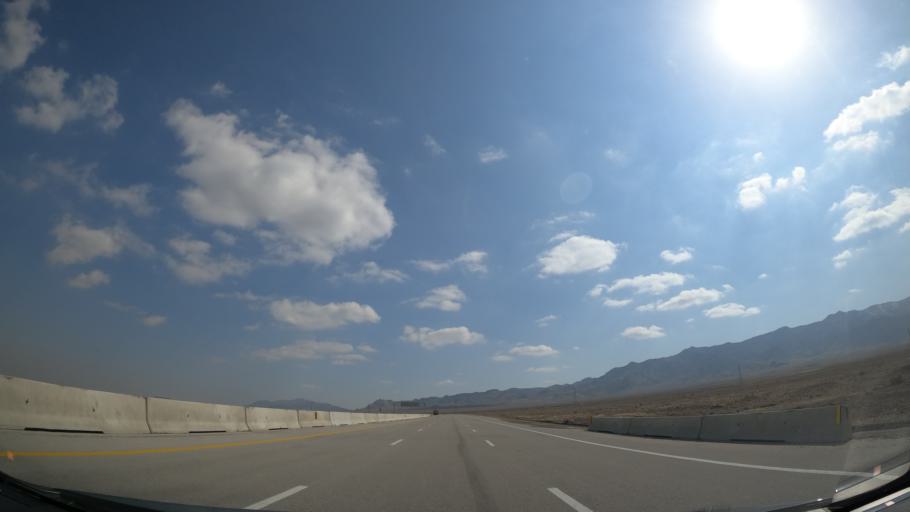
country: IR
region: Alborz
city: Eshtehard
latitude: 35.7205
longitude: 50.5702
